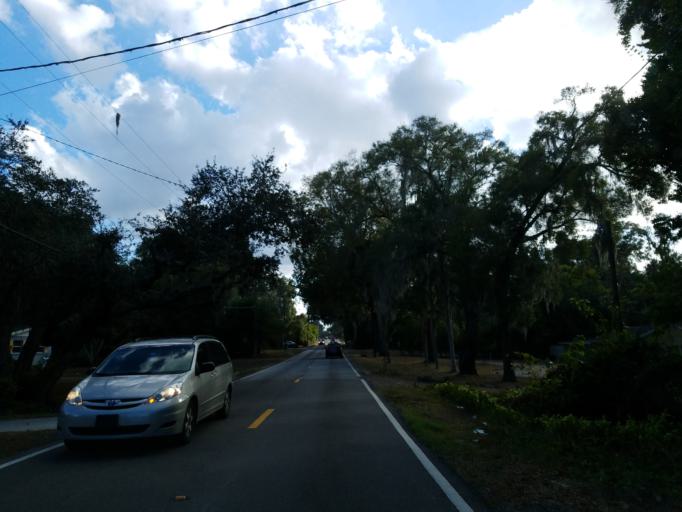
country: US
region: Florida
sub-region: Hillsborough County
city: Brandon
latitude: 27.9489
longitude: -82.3042
